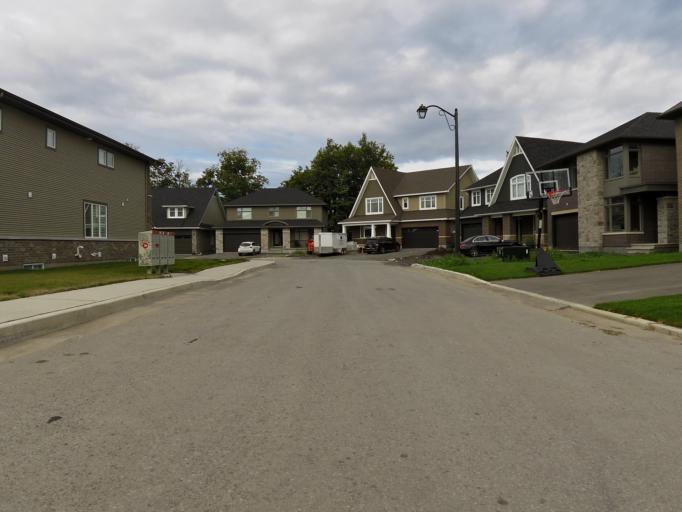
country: CA
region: Ontario
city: Bells Corners
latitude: 45.3204
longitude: -75.9396
